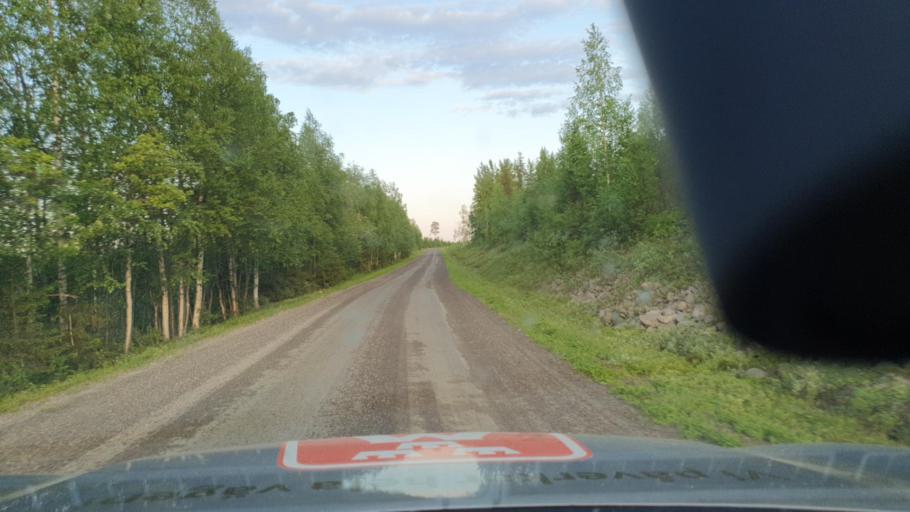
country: SE
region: Norrbotten
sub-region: Bodens Kommun
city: Boden
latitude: 66.4767
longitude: 21.6193
